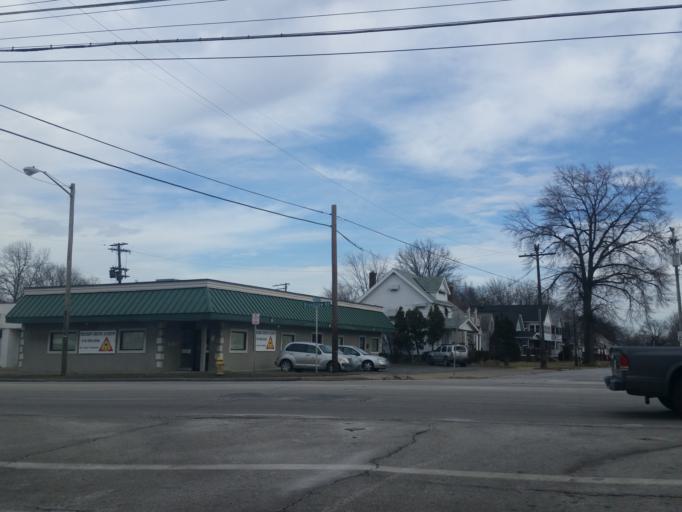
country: US
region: Ohio
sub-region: Cuyahoga County
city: Brooklyn Heights
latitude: 41.4154
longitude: -81.6943
